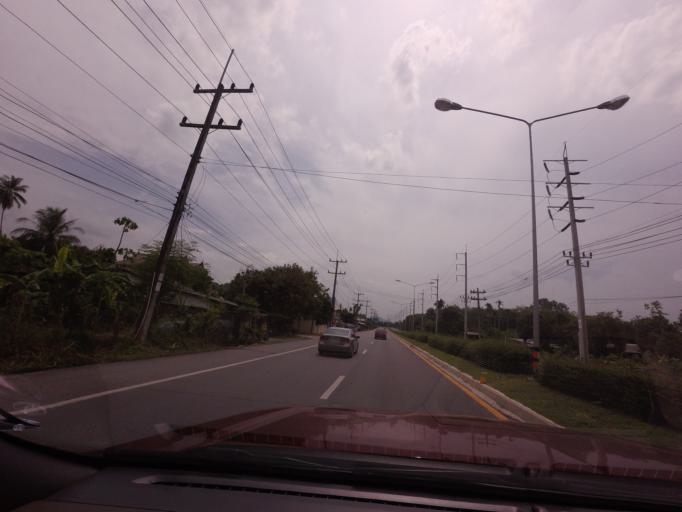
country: TH
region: Yala
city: Yala
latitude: 6.4994
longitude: 101.2798
